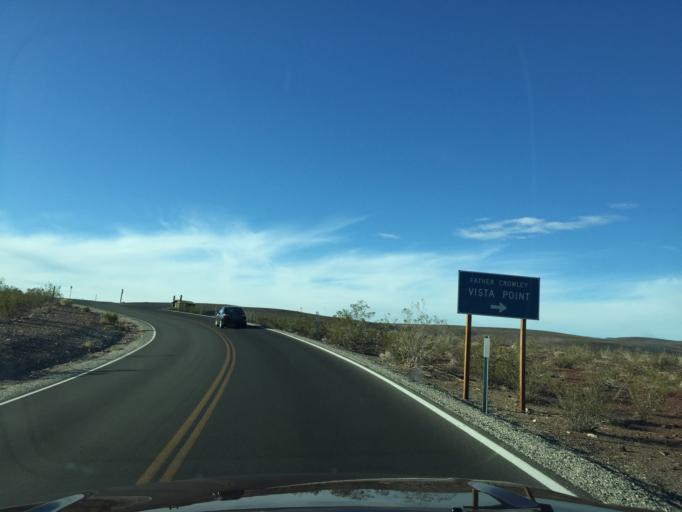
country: US
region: California
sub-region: Inyo County
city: Lone Pine
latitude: 36.3507
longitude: -117.5503
